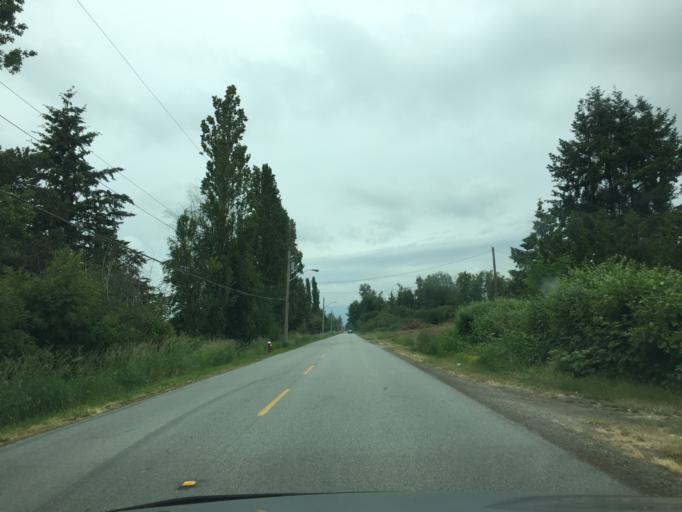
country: CA
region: British Columbia
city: Ladner
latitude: 49.1430
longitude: -123.0808
